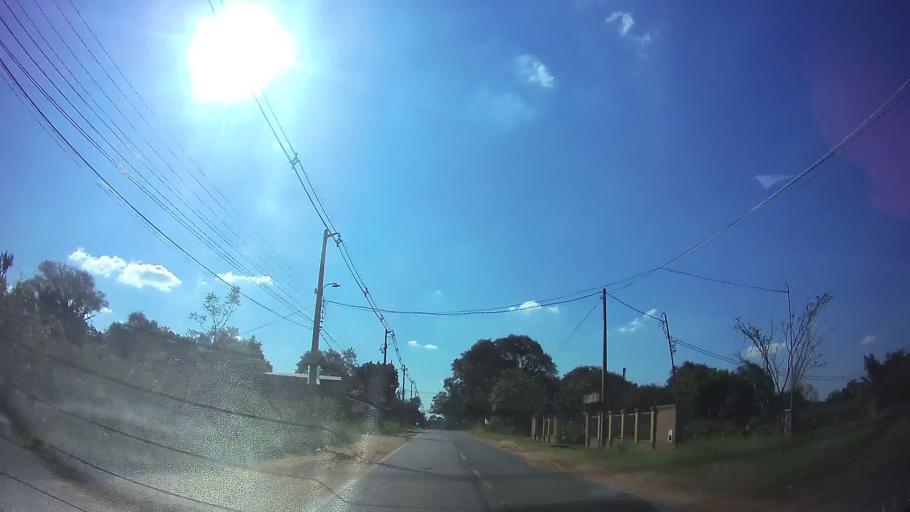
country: PY
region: Central
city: Limpio
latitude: -25.2284
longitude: -57.4766
